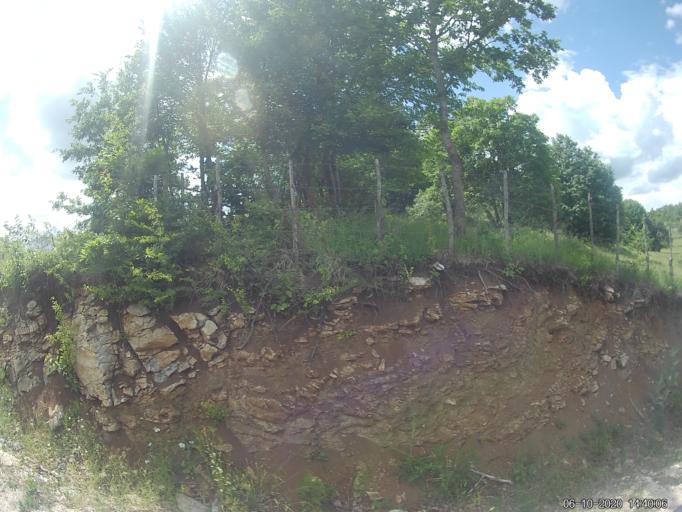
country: XK
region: Prizren
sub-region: Komuna e Therandes
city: Budakovo
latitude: 42.3979
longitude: 20.9433
